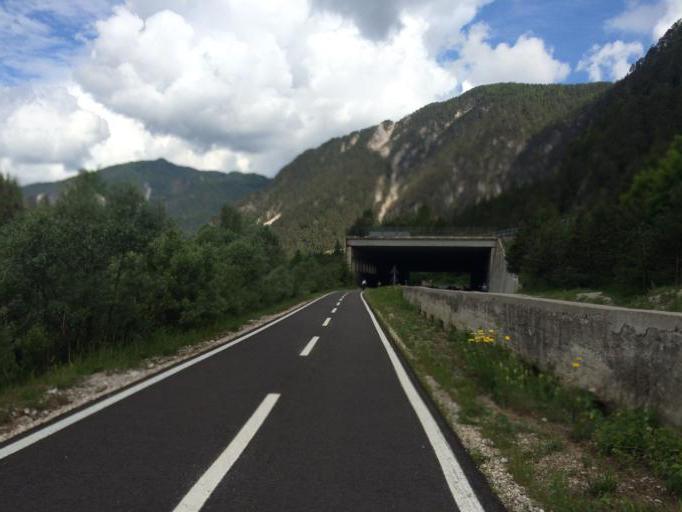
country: IT
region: Friuli Venezia Giulia
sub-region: Provincia di Udine
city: Malborghetto
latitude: 46.5030
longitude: 13.4960
